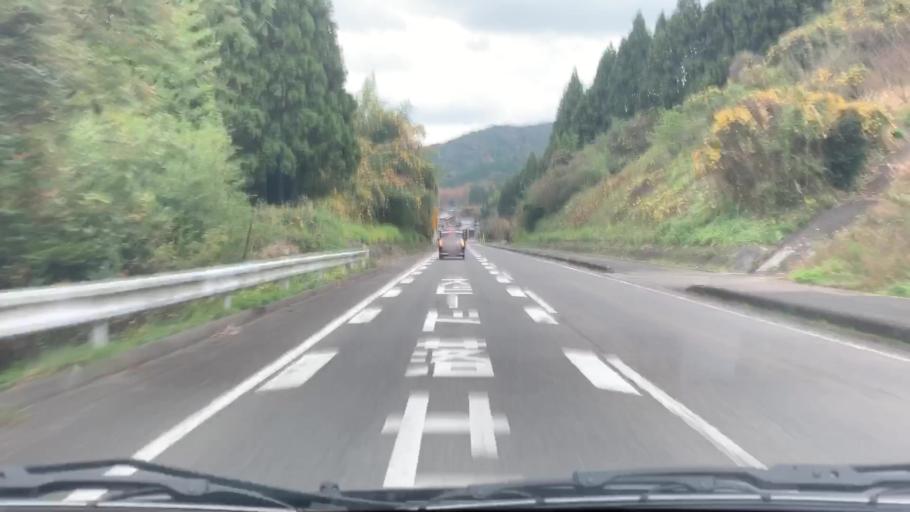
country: JP
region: Saga Prefecture
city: Kashima
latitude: 33.0988
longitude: 130.0466
